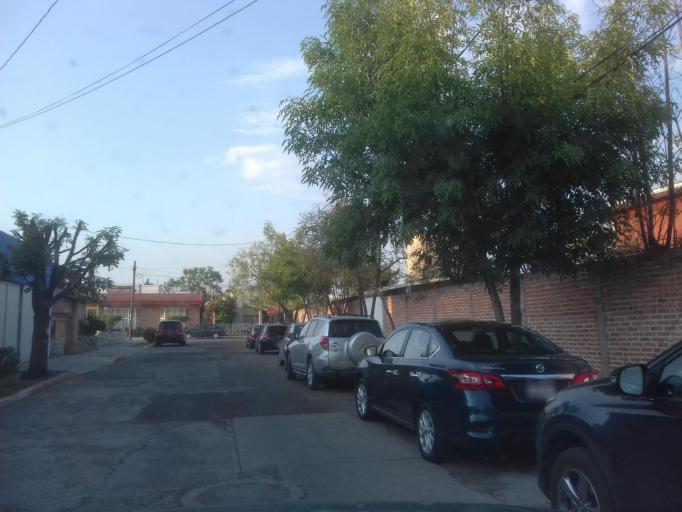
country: MX
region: Aguascalientes
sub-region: Aguascalientes
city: Aguascalientes
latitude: 21.8642
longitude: -102.2870
